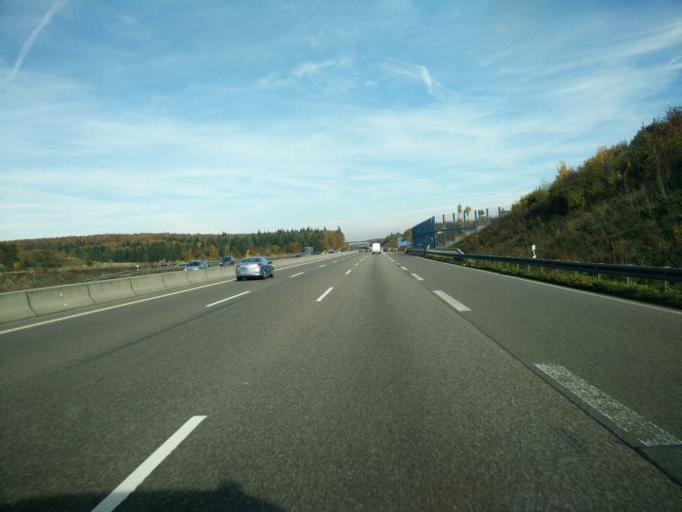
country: DE
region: Baden-Wuerttemberg
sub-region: Karlsruhe Region
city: Wurmberg
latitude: 48.8778
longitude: 8.7887
